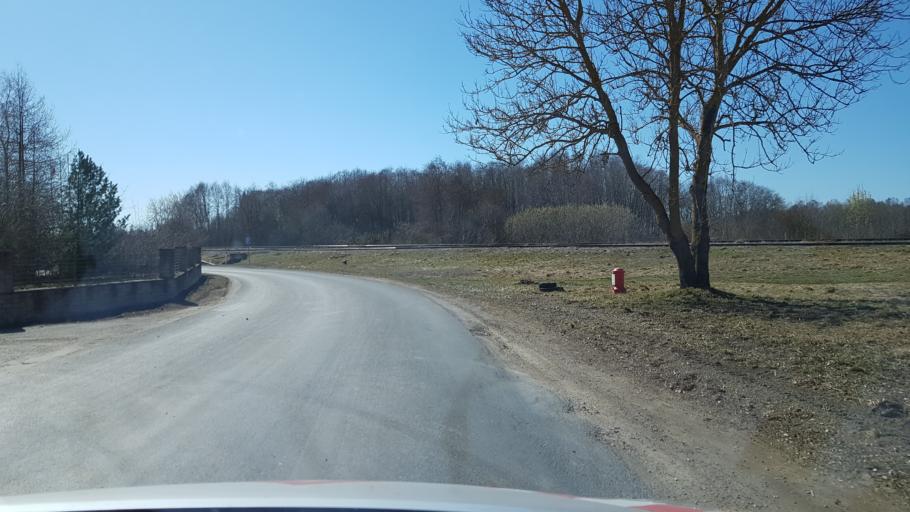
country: EE
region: Laeaene-Virumaa
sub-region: Someru vald
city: Someru
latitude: 59.3644
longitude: 26.3969
